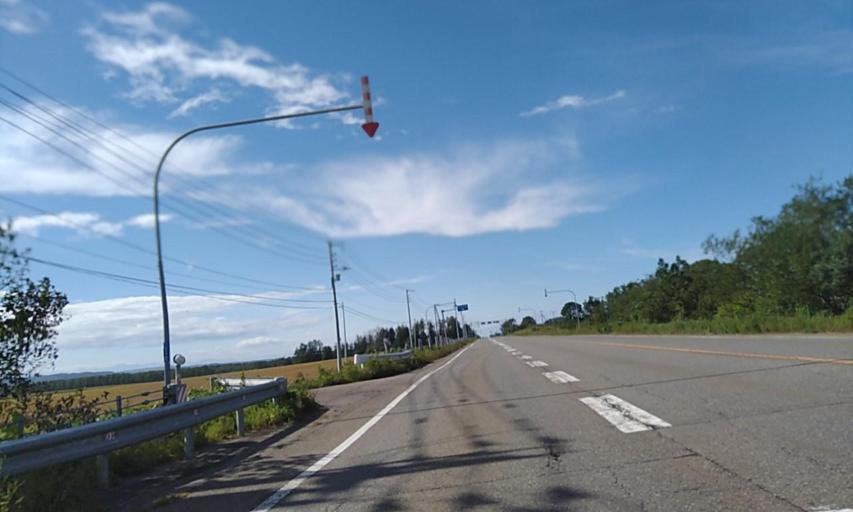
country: JP
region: Hokkaido
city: Obihiro
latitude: 42.7993
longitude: 143.5724
